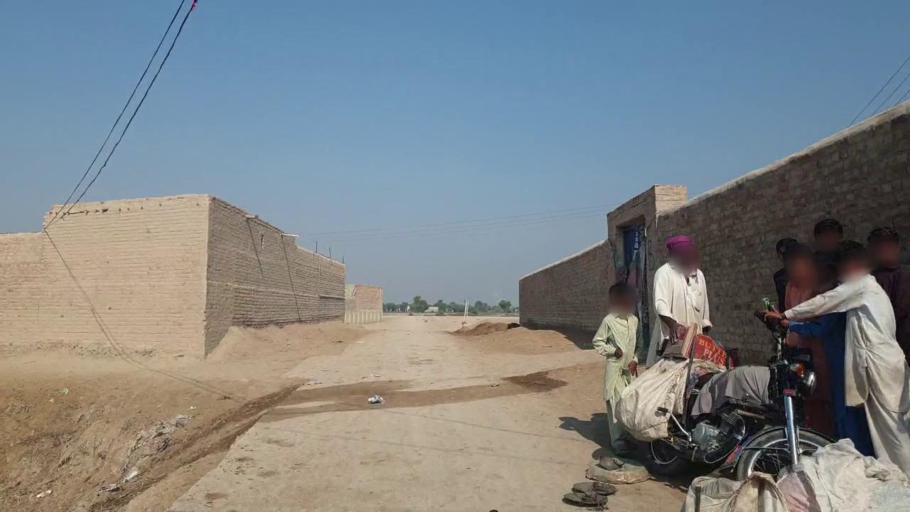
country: PK
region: Sindh
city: Bhan
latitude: 26.4410
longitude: 67.7320
